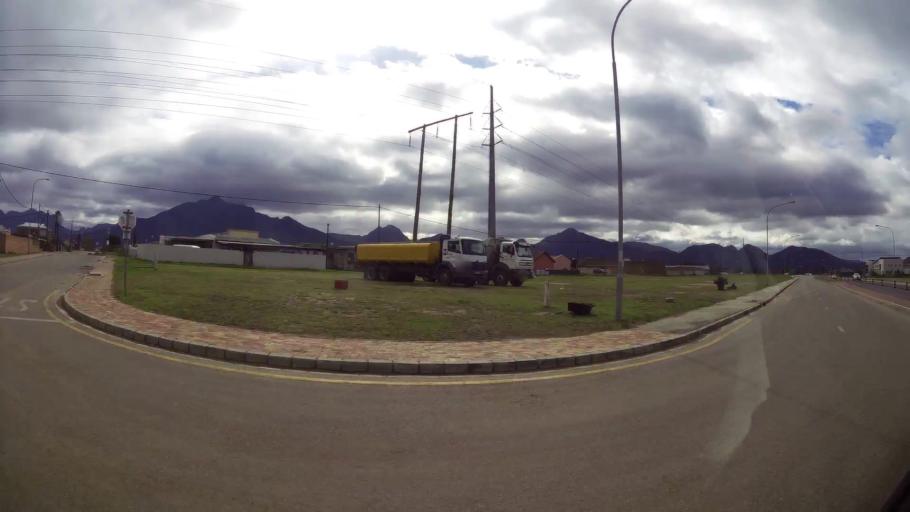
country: ZA
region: Western Cape
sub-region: Eden District Municipality
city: George
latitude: -33.9795
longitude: 22.4924
